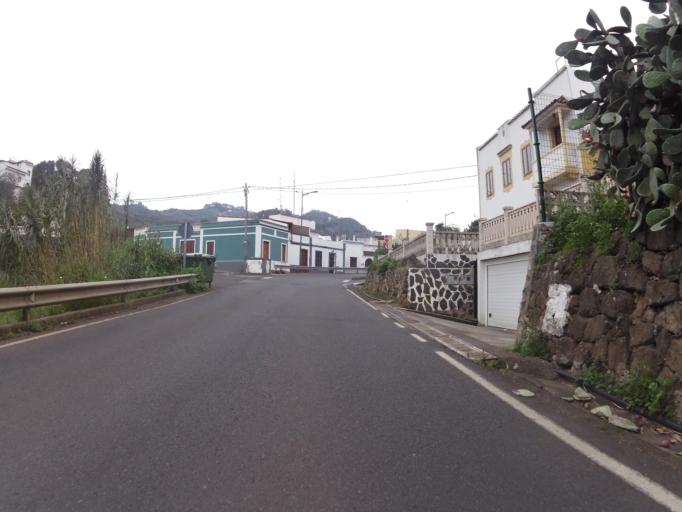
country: ES
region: Canary Islands
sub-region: Provincia de Las Palmas
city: Teror
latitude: 28.0638
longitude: -15.5387
